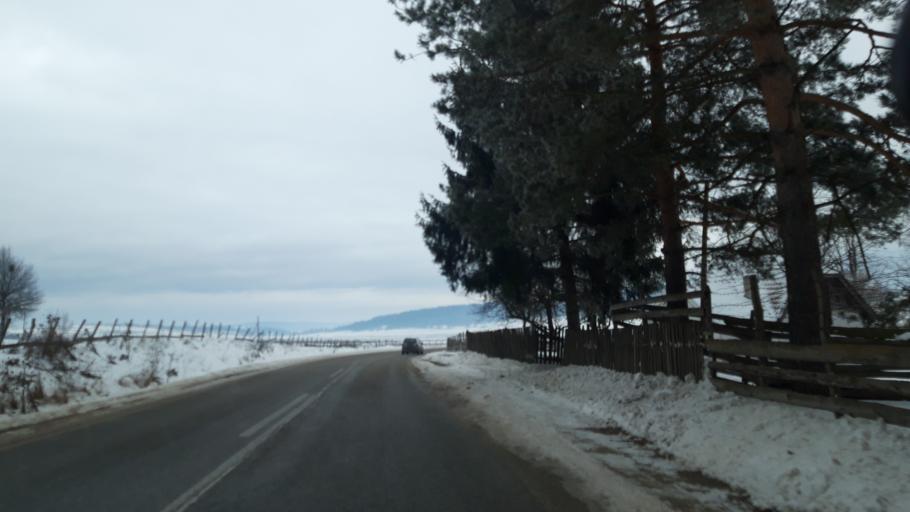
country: BA
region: Republika Srpska
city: Sokolac
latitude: 43.9621
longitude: 18.8563
